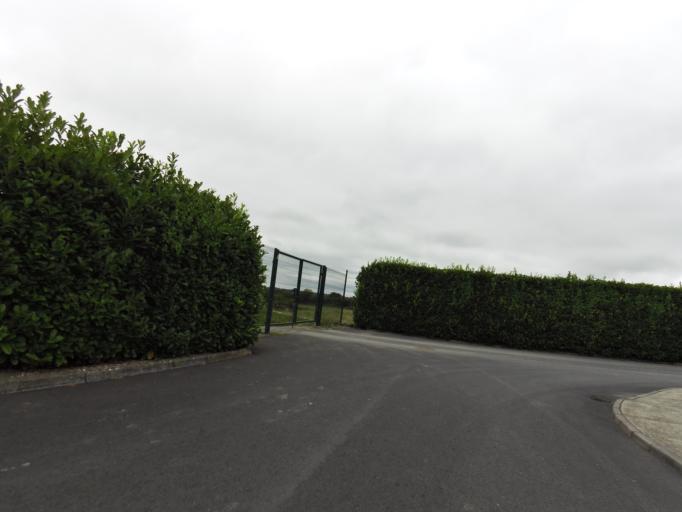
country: IE
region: Connaught
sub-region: County Galway
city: Loughrea
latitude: 53.2061
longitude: -8.5616
